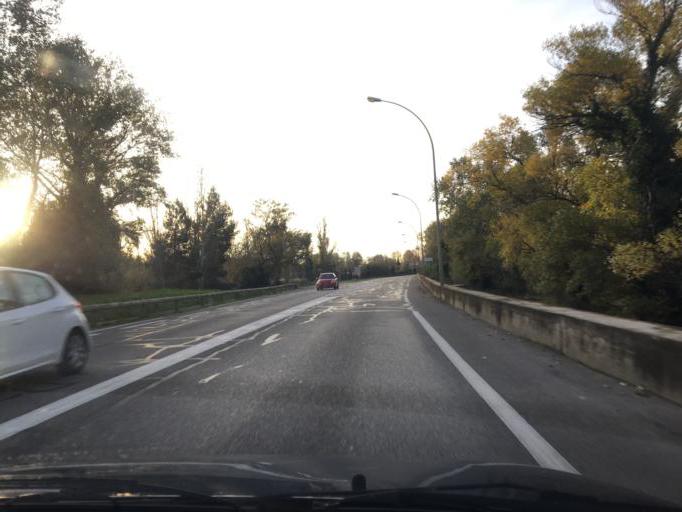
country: FR
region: Provence-Alpes-Cote d'Azur
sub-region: Departement du Vaucluse
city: Cavaillon
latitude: 43.8255
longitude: 5.0359
